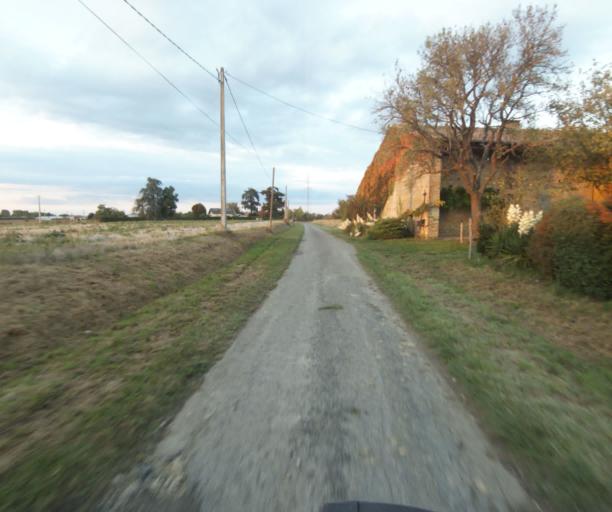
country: FR
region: Midi-Pyrenees
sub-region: Departement du Tarn-et-Garonne
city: Verdun-sur-Garonne
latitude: 43.8360
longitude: 1.2455
